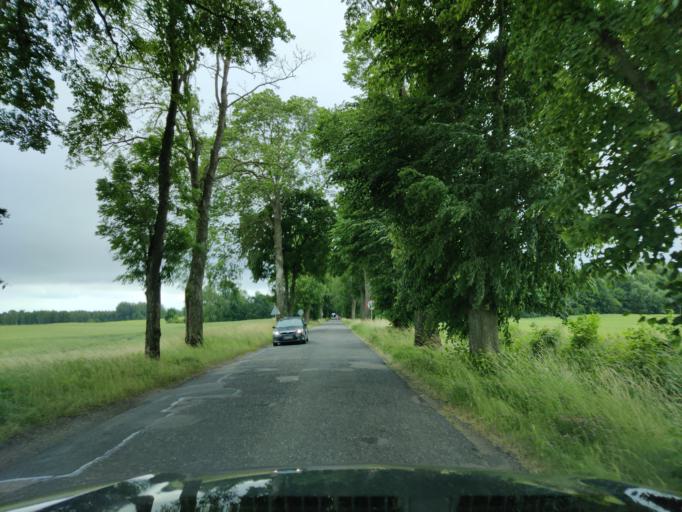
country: PL
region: Warmian-Masurian Voivodeship
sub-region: Powiat gizycki
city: Ryn
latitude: 53.9194
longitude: 21.5545
